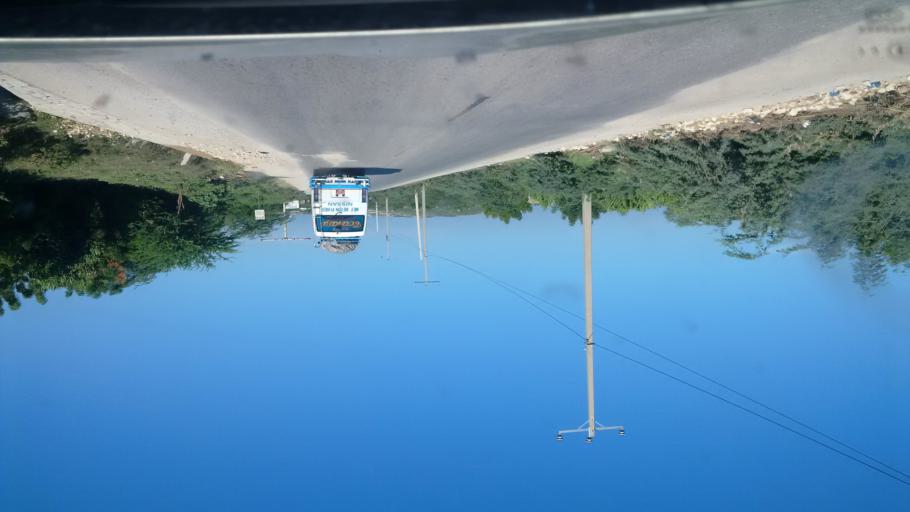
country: HT
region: Ouest
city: Cabaret
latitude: 18.7152
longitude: -72.3615
